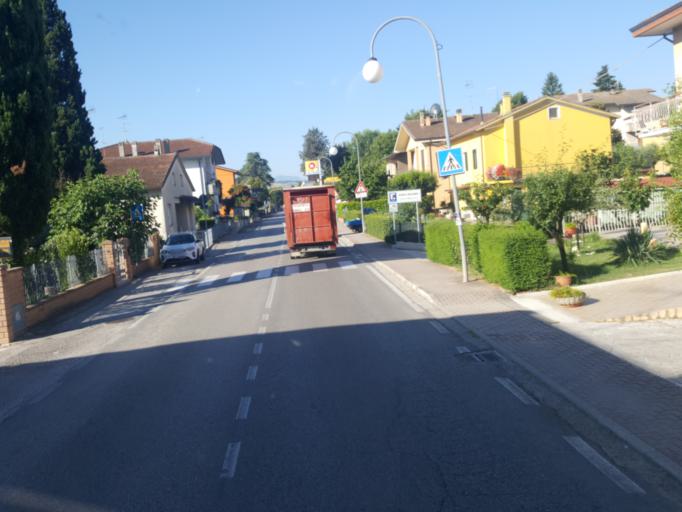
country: IT
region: The Marches
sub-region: Provincia di Pesaro e Urbino
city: Borgo Massano
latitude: 43.8185
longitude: 12.6663
